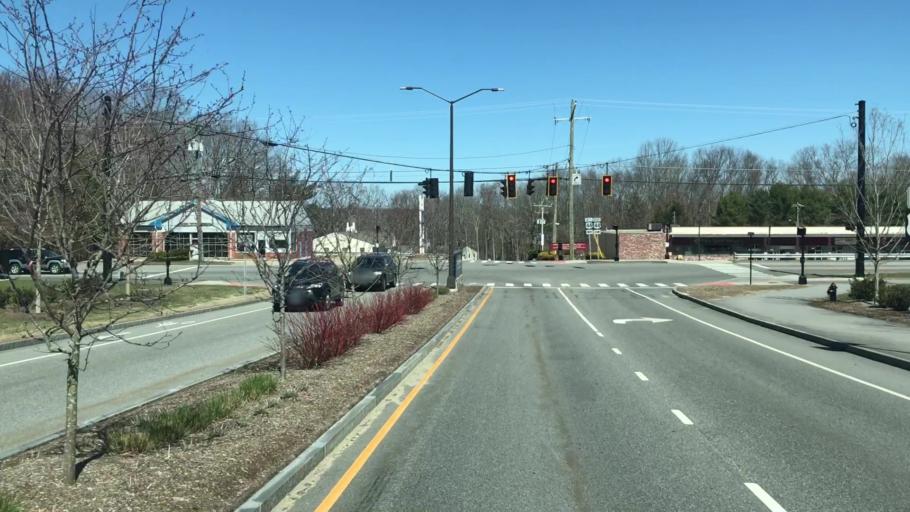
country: US
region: Connecticut
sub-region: Tolland County
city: Storrs
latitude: 41.8249
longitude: -72.2709
